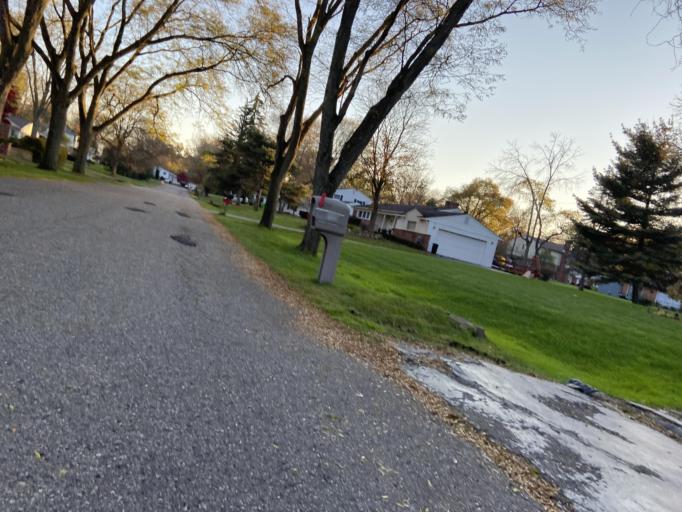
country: US
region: Michigan
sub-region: Oakland County
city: Franklin
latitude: 42.5338
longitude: -83.3365
